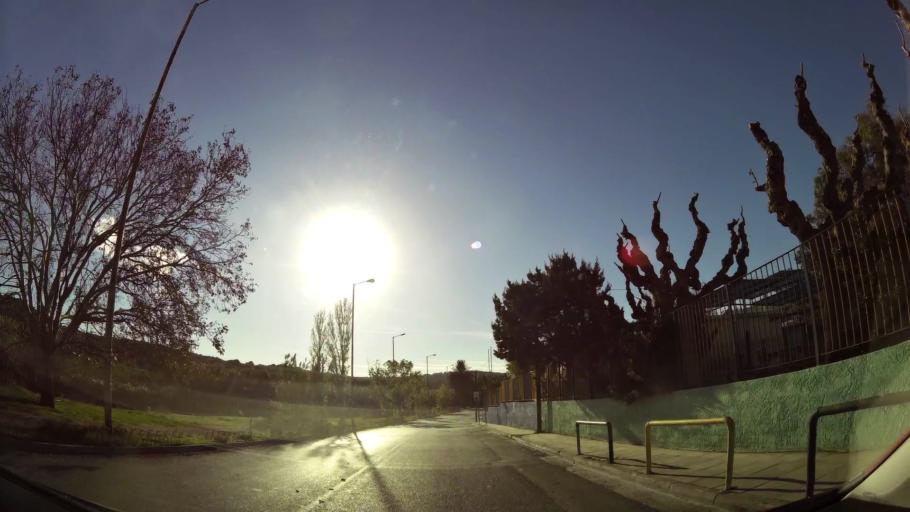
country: GR
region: Attica
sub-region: Nomarchia Anatolikis Attikis
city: Rafina
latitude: 38.0176
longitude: 24.0090
